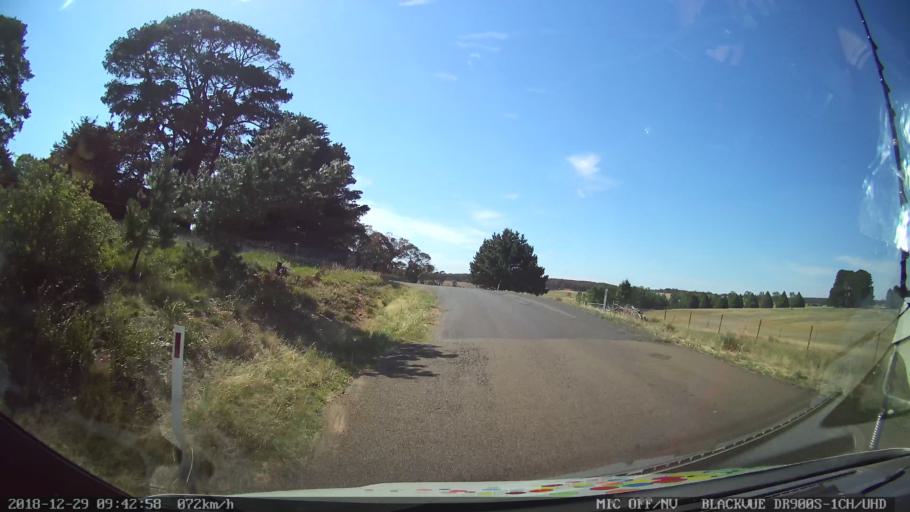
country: AU
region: New South Wales
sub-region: Upper Lachlan Shire
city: Crookwell
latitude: -34.6750
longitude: 149.4236
